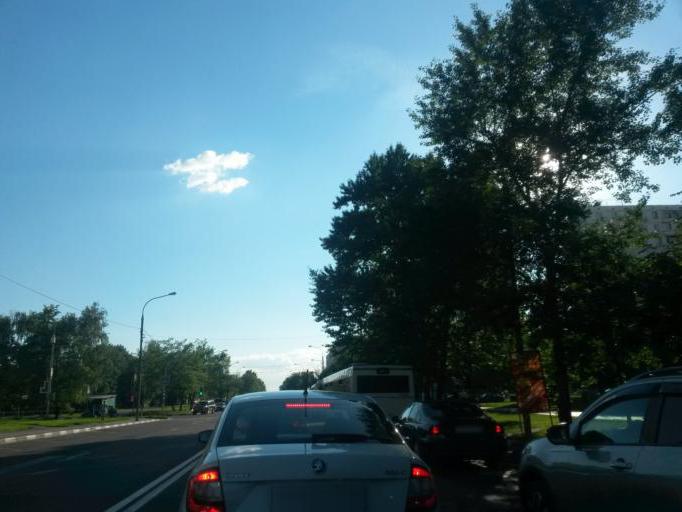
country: RU
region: Moscow
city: Orekhovo-Borisovo
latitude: 55.6043
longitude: 37.7360
